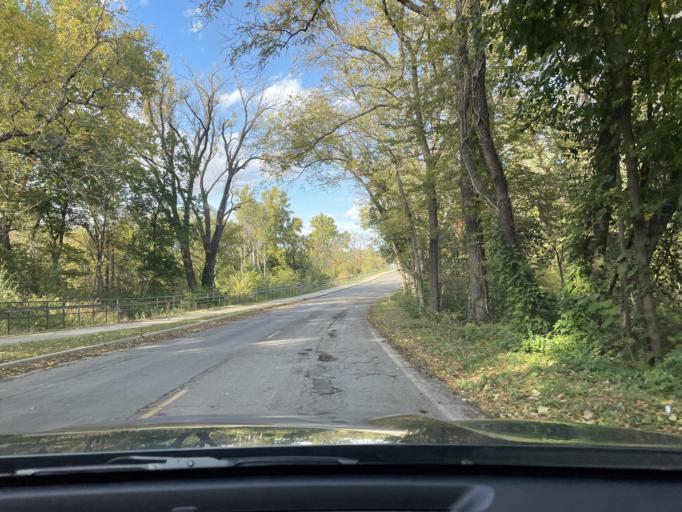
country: US
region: Missouri
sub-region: Buchanan County
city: Saint Joseph
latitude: 39.7339
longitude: -94.8386
